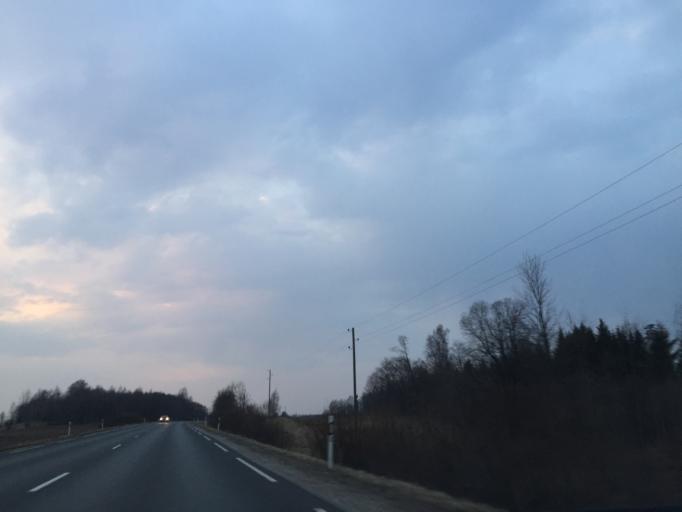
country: LV
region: Raunas
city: Rauna
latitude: 57.2399
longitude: 25.5611
